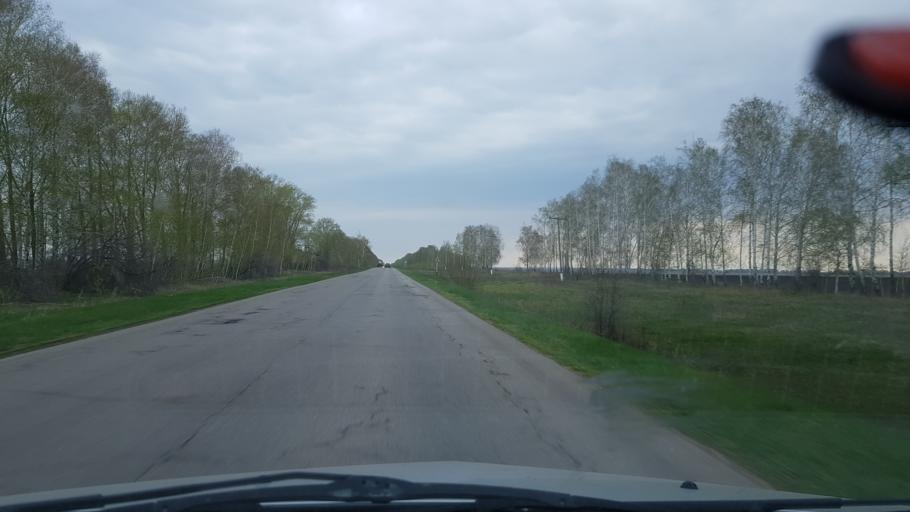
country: RU
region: Samara
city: Podstepki
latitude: 53.6606
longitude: 49.2178
